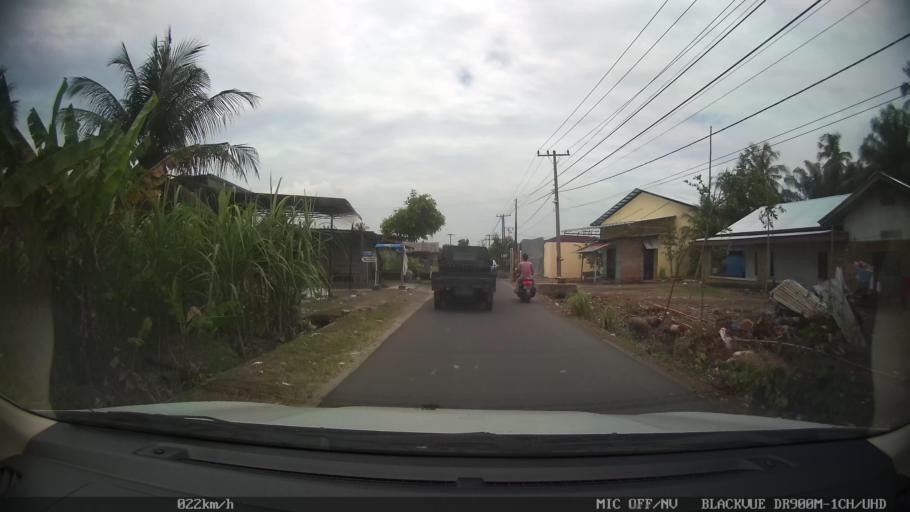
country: ID
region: North Sumatra
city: Binjai
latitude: 3.6236
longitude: 98.5553
